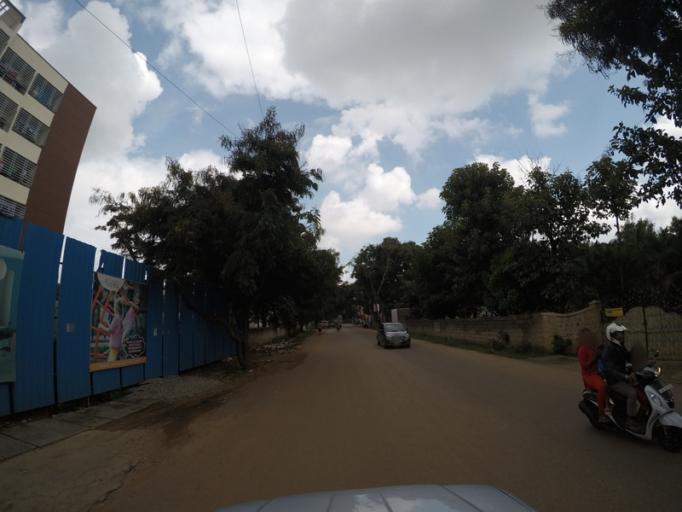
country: IN
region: Karnataka
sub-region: Bangalore Urban
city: Yelahanka
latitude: 13.0906
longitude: 77.5392
